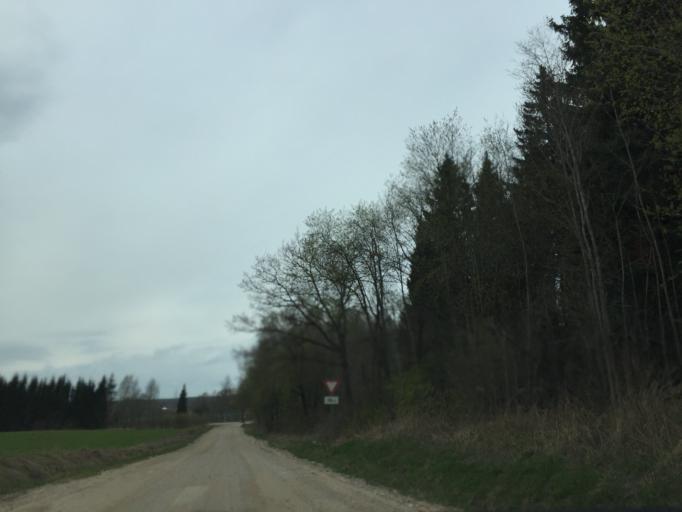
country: LV
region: Priekuli
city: Priekuli
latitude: 57.3444
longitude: 25.3466
